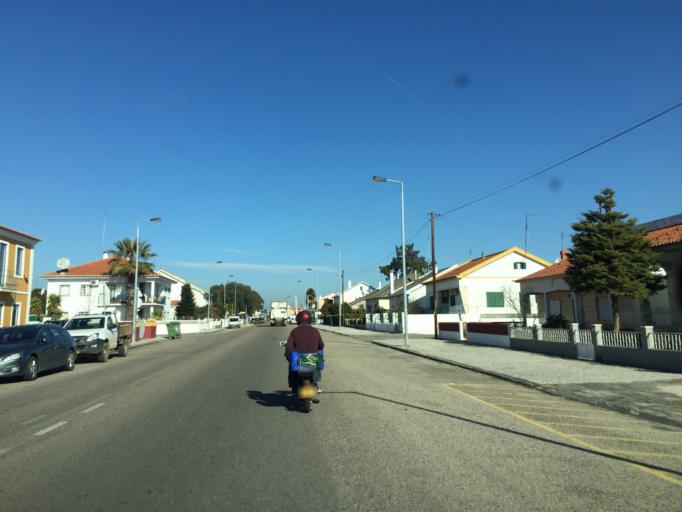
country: PT
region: Portalegre
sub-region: Ponte de Sor
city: Ponte de Sor
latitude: 39.2559
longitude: -8.0103
